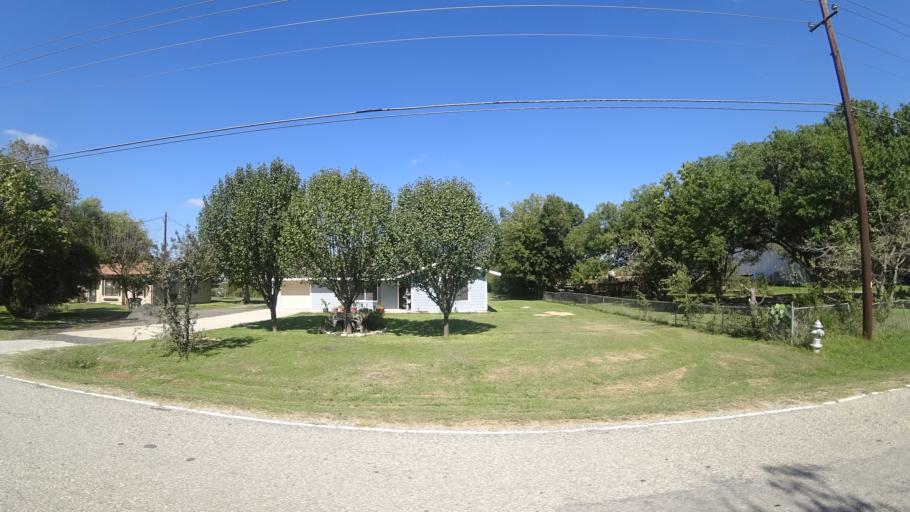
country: US
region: Texas
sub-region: Travis County
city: Manor
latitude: 30.3389
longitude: -97.6060
